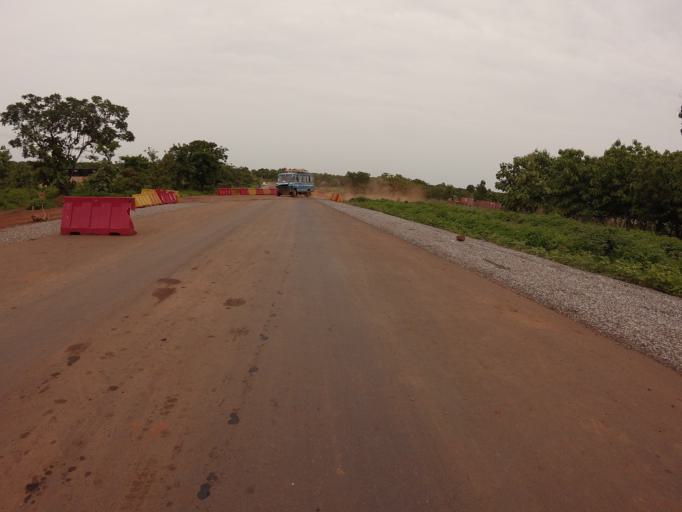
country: GH
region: Northern
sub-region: Yendi
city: Yendi
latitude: 9.0666
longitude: -0.0112
